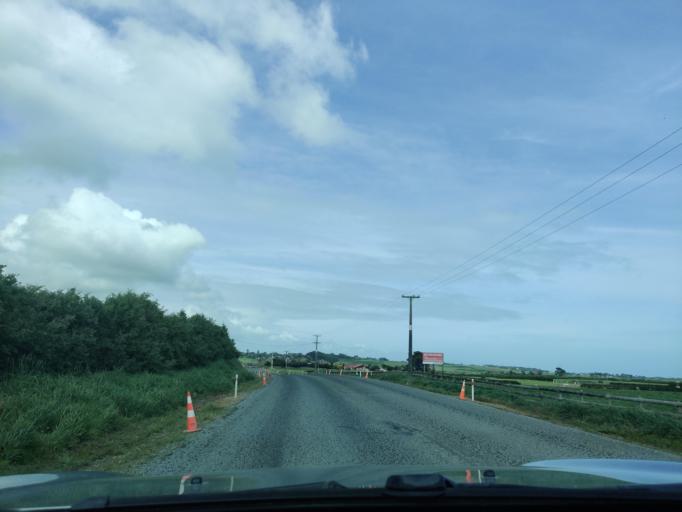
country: NZ
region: Taranaki
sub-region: South Taranaki District
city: Hawera
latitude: -39.5841
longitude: 174.2404
